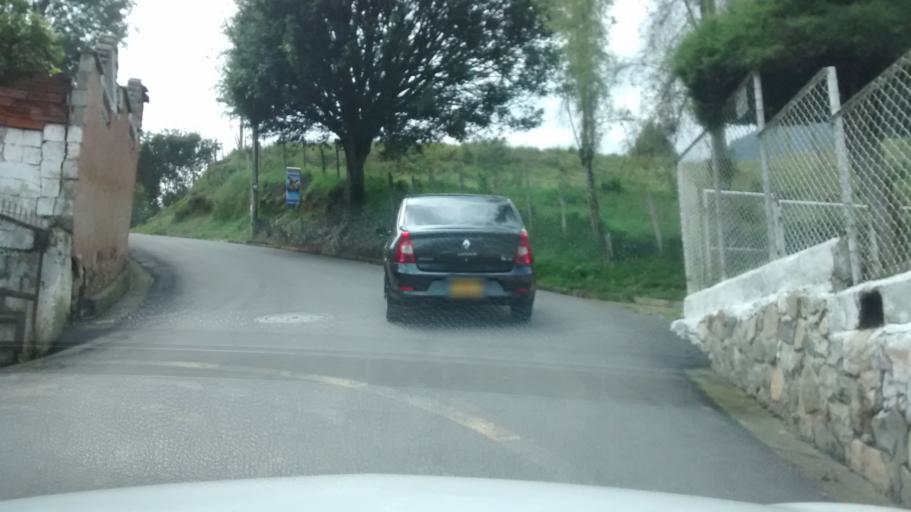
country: CO
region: Antioquia
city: La Estrella
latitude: 6.1766
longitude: -75.6609
